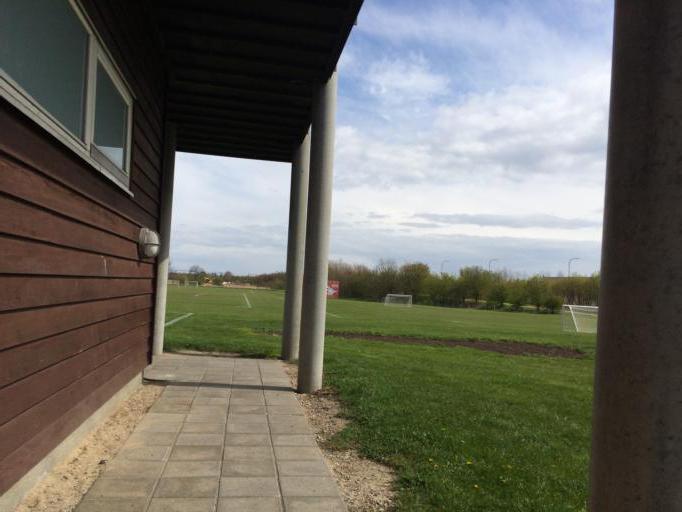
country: DK
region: Capital Region
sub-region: Ishoj Kommune
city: Ishoj
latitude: 55.6046
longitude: 12.3374
